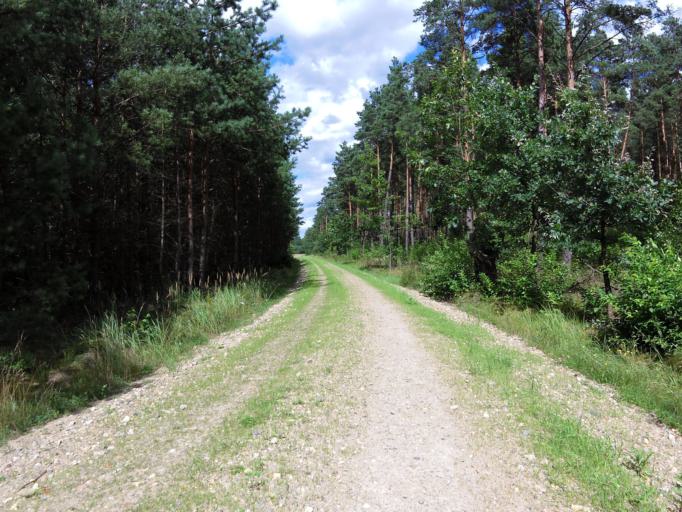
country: DE
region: Brandenburg
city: Lychen
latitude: 53.1625
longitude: 13.3804
